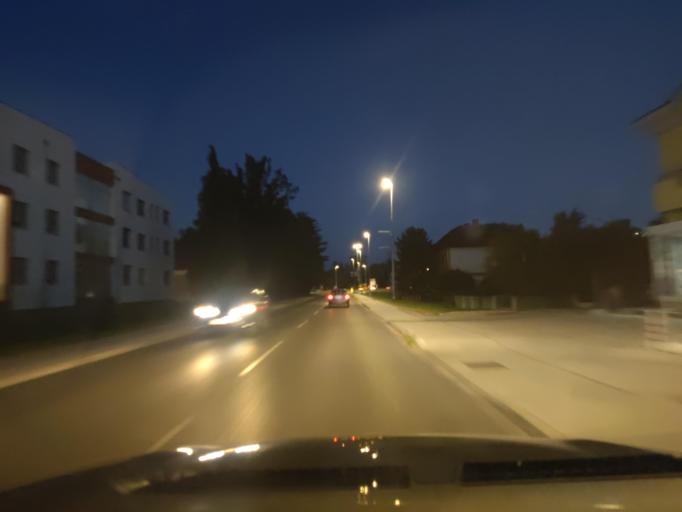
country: HR
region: Medimurska
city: Cakovec
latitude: 46.3934
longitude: 16.4326
